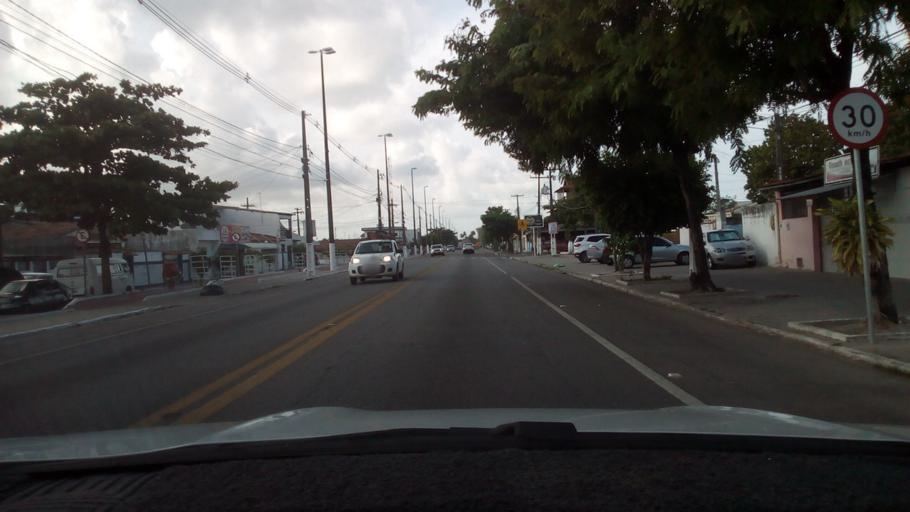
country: BR
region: Paraiba
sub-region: Cabedelo
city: Cabedelo
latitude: -6.9793
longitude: -34.8306
